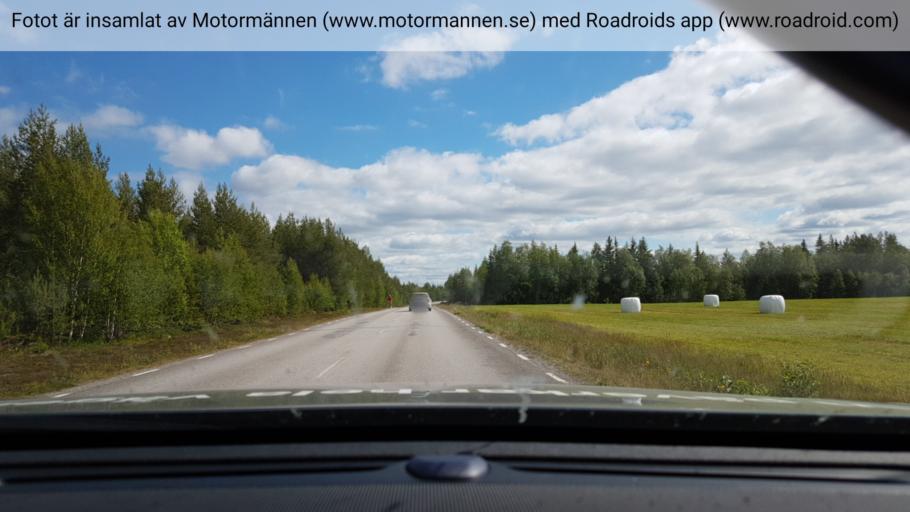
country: SE
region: Vaesterbotten
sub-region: Sorsele Kommun
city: Sorsele
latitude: 65.5950
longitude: 17.5027
